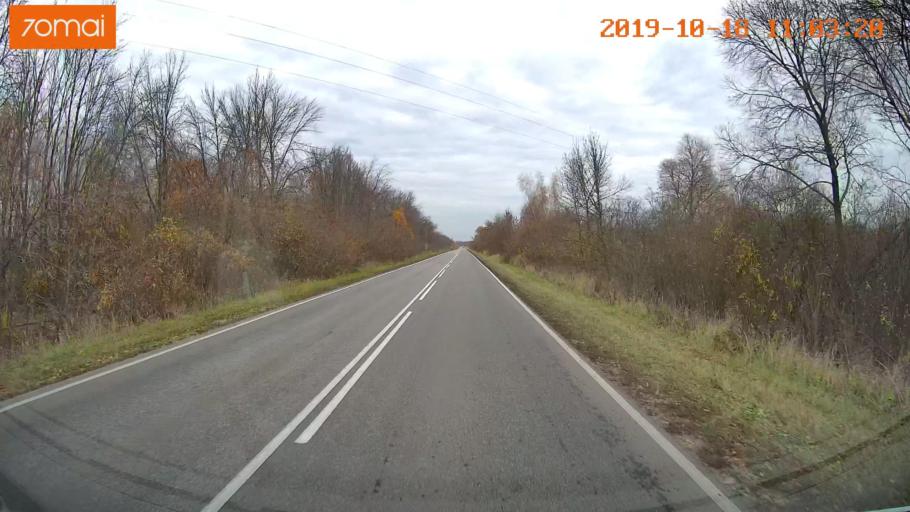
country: RU
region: Tula
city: Yepifan'
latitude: 53.8781
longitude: 38.5483
